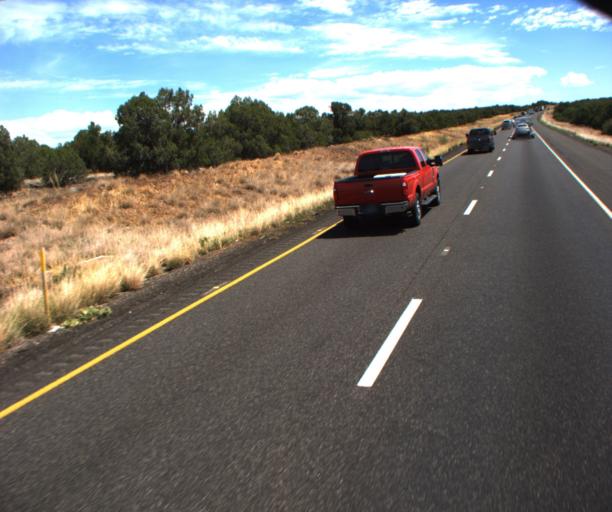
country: US
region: Arizona
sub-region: Yavapai County
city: Big Park
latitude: 34.7361
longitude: -111.6960
